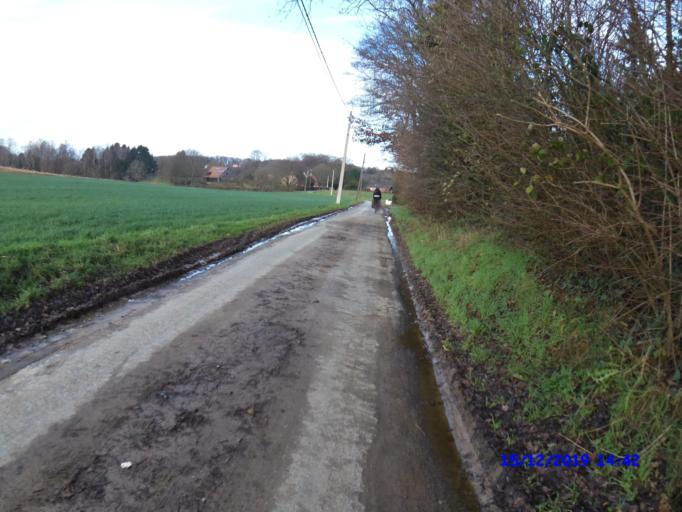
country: BE
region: Flanders
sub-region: Provincie Vlaams-Brabant
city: Beersel
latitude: 50.7461
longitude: 4.3136
